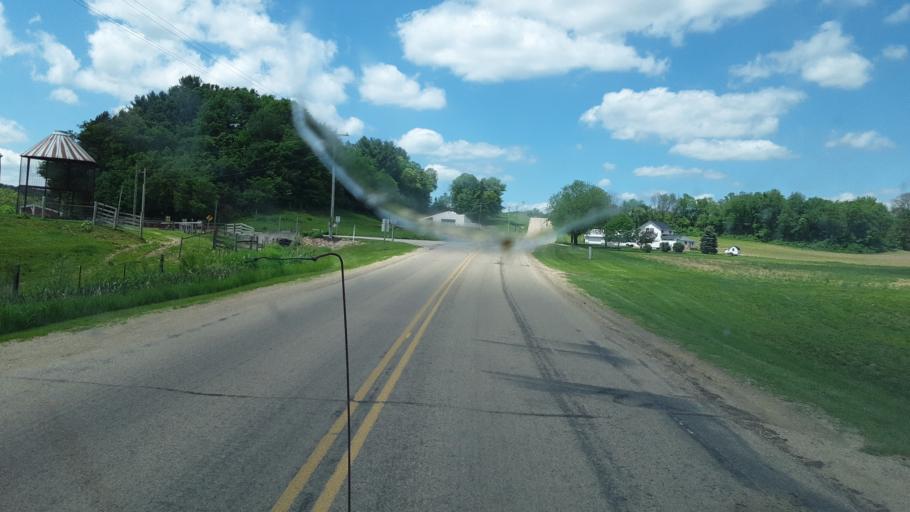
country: US
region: Wisconsin
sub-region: Sauk County
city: Reedsburg
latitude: 43.5750
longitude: -89.9995
